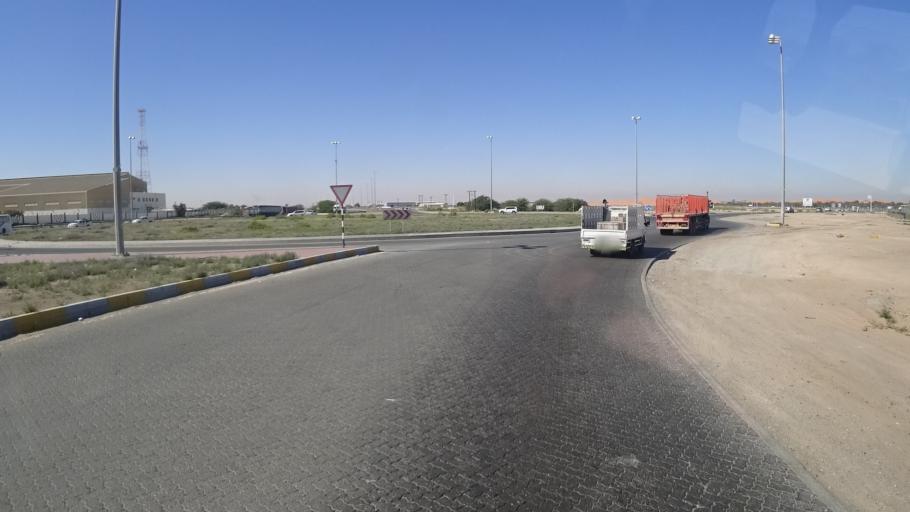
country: AE
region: Abu Dhabi
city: Al Ain
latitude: 24.0799
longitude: 55.6650
